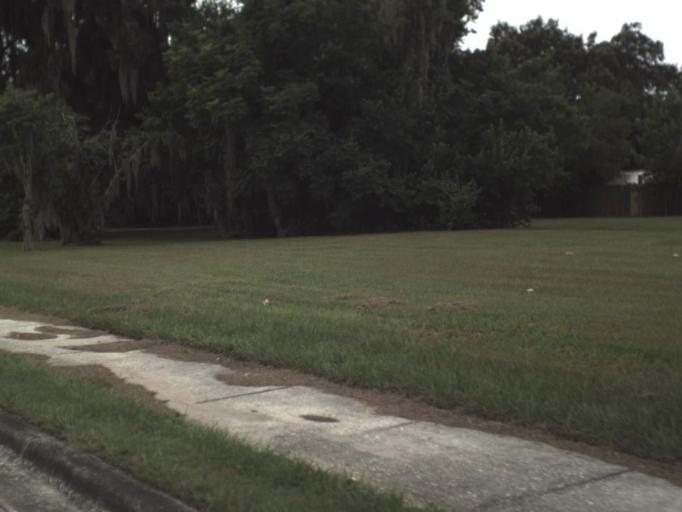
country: US
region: Florida
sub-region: Polk County
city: Bartow
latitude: 27.8761
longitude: -81.8287
